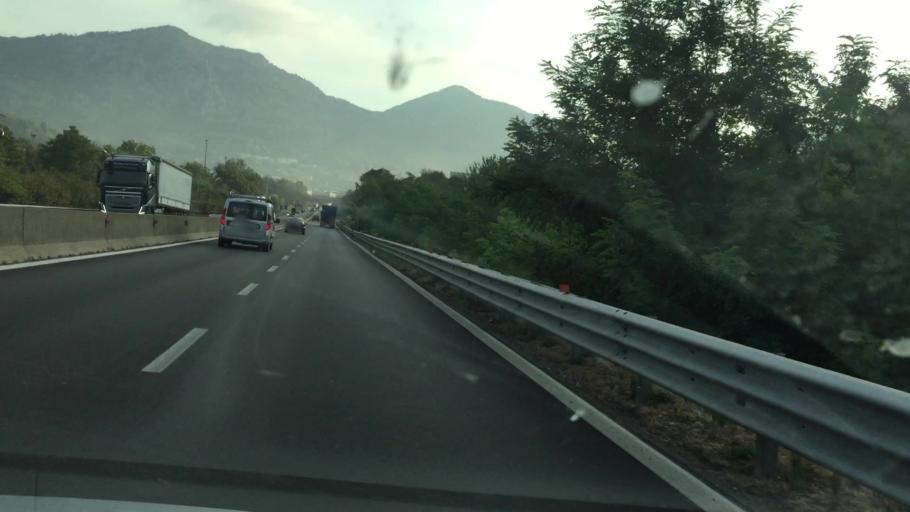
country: IT
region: Campania
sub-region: Provincia di Avellino
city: Torchiati
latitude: 40.8270
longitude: 14.8135
